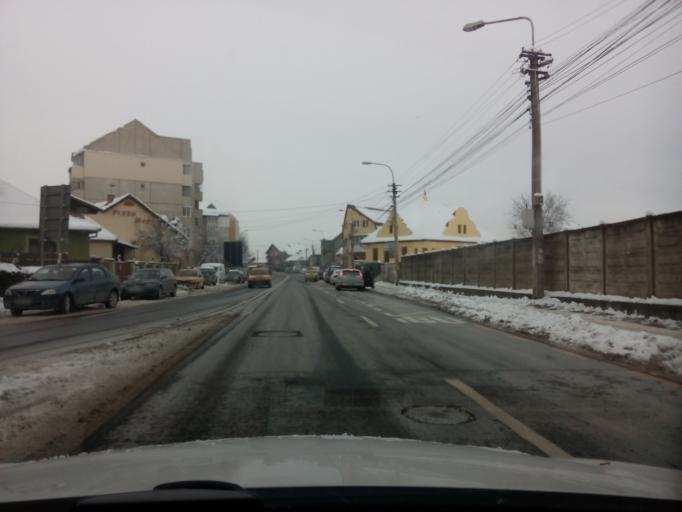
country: RO
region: Sibiu
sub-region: Municipiul Sibiu
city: Sibiu
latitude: 45.8056
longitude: 24.1519
